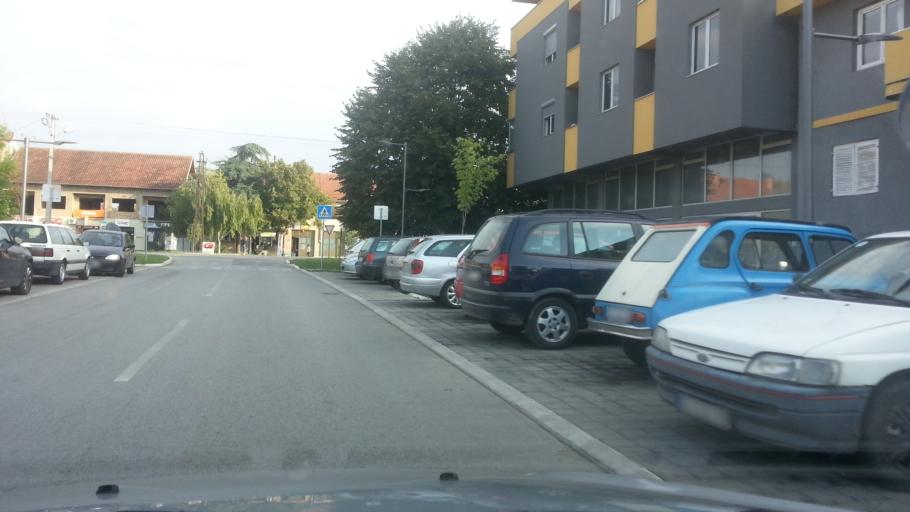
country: RS
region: Autonomna Pokrajina Vojvodina
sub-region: Sremski Okrug
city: Stara Pazova
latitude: 44.9838
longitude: 20.1559
